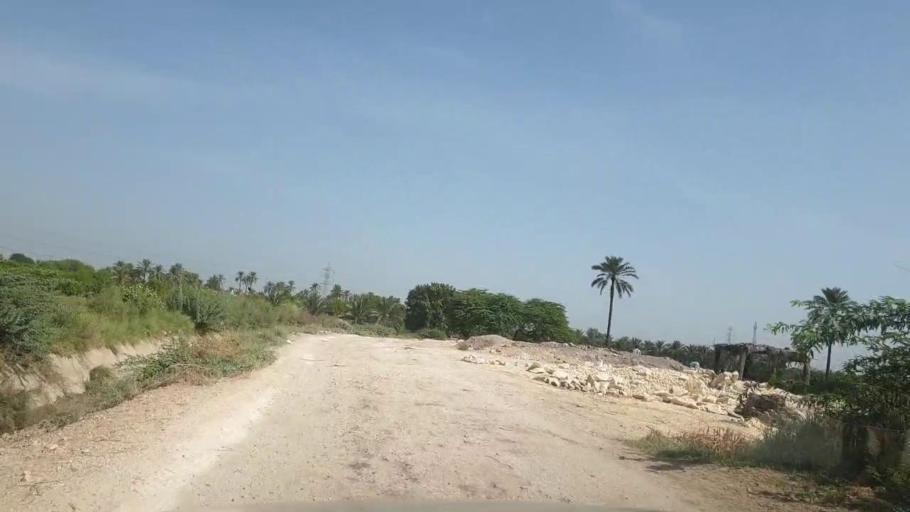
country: PK
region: Sindh
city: Rohri
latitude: 27.6654
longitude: 68.8834
